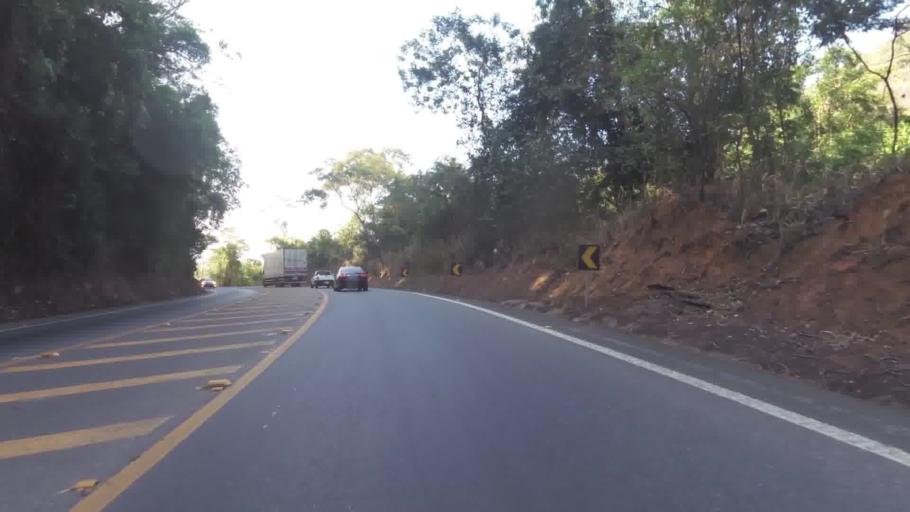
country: BR
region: Espirito Santo
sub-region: Alfredo Chaves
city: Alfredo Chaves
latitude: -20.7090
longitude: -40.7184
